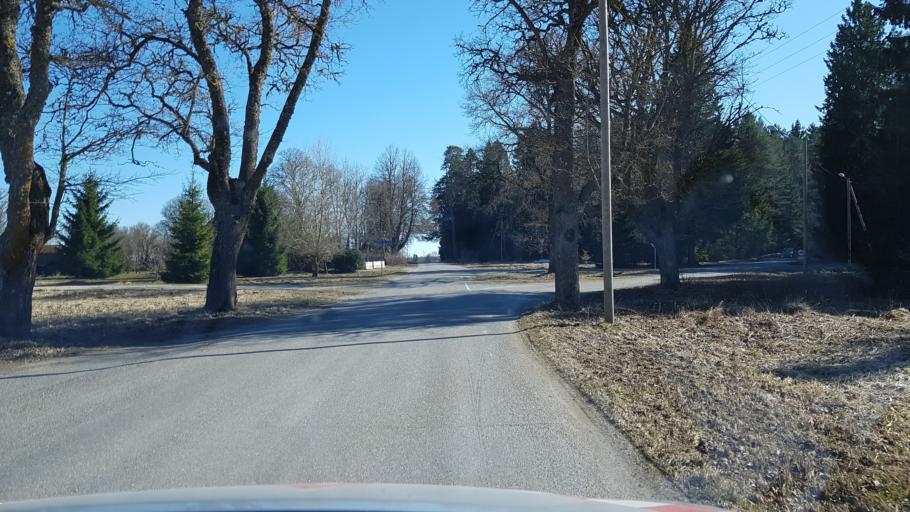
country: EE
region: Laeaene-Virumaa
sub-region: Viru-Nigula vald
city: Kunda
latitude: 59.4117
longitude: 26.5306
